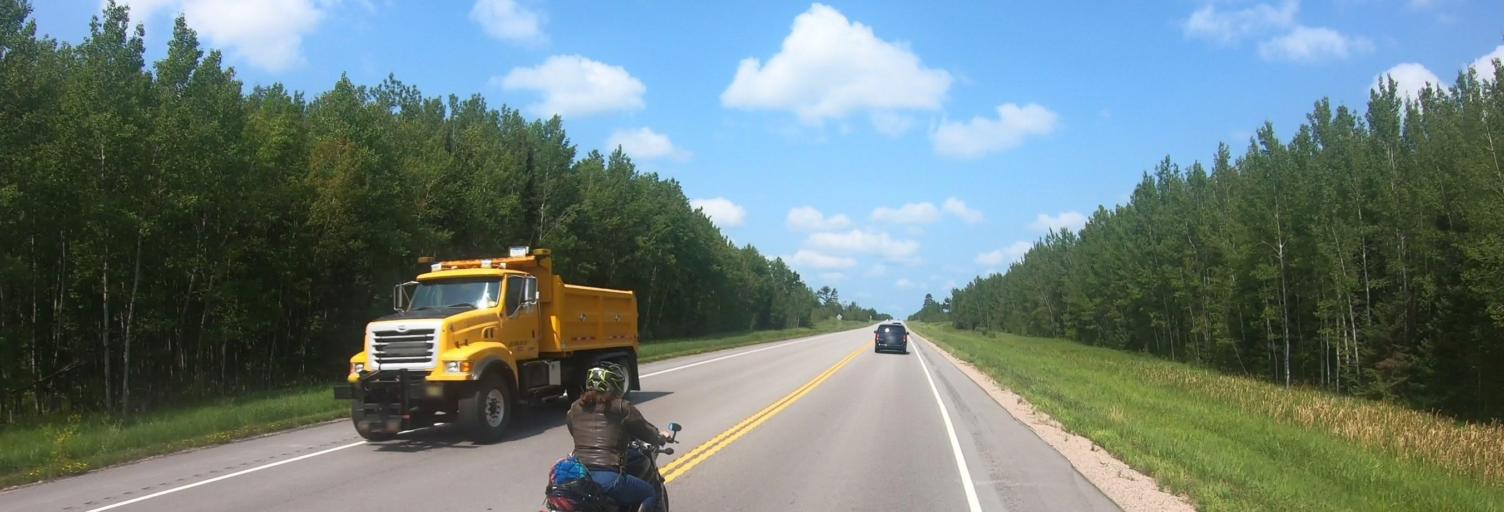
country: US
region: Minnesota
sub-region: Saint Louis County
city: Mountain Iron
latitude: 47.8975
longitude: -92.7825
